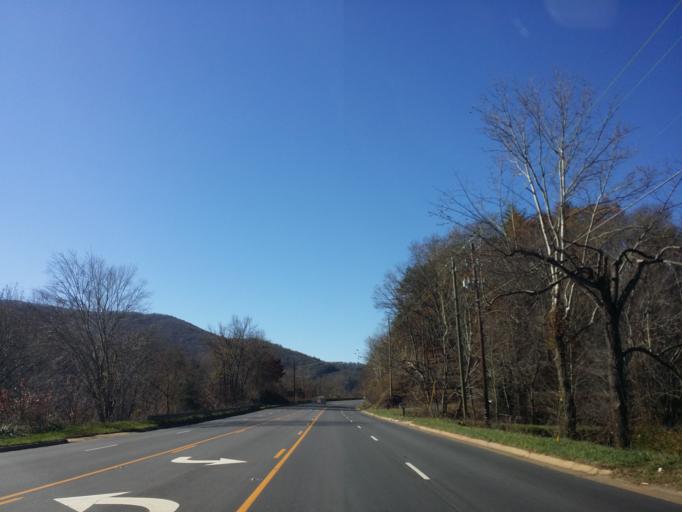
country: US
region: North Carolina
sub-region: Buncombe County
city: Swannanoa
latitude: 35.5882
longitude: -82.4552
